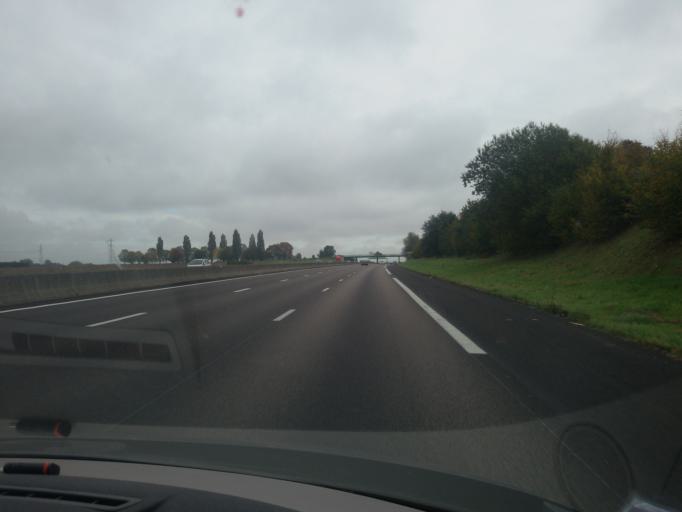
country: FR
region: Haute-Normandie
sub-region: Departement de l'Eure
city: Corneville-sur-Risle
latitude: 49.3749
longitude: 0.6447
